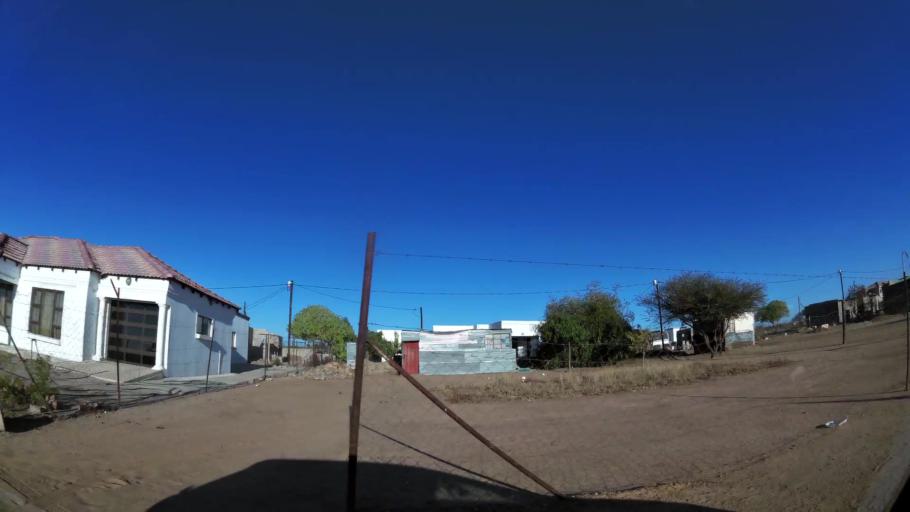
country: ZA
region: Limpopo
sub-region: Capricorn District Municipality
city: Polokwane
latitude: -23.8383
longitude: 29.3636
